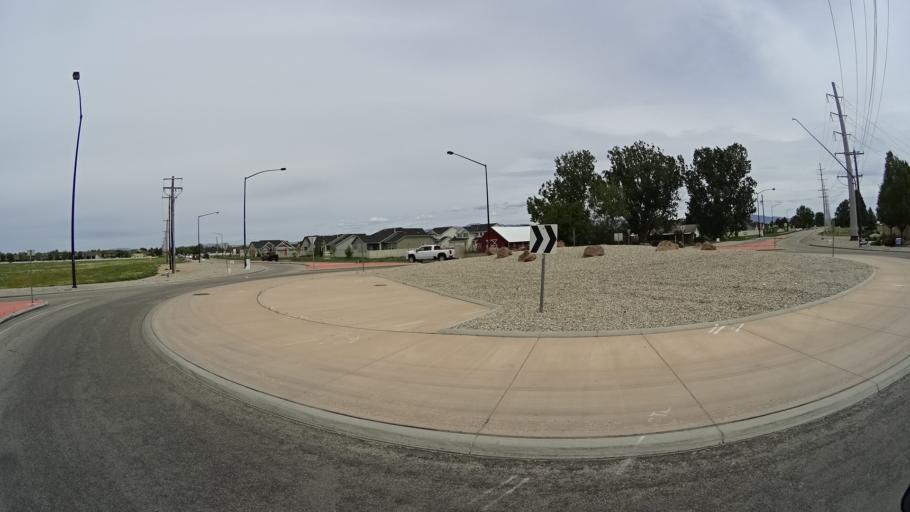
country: US
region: Idaho
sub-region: Ada County
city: Meridian
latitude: 43.5608
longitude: -116.3548
